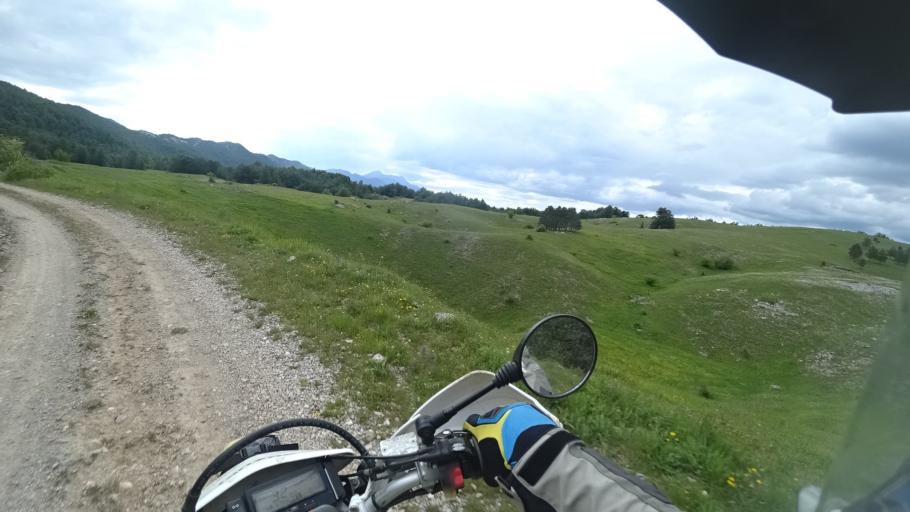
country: HR
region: Zadarska
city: Obrovac
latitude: 44.2787
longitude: 15.7231
